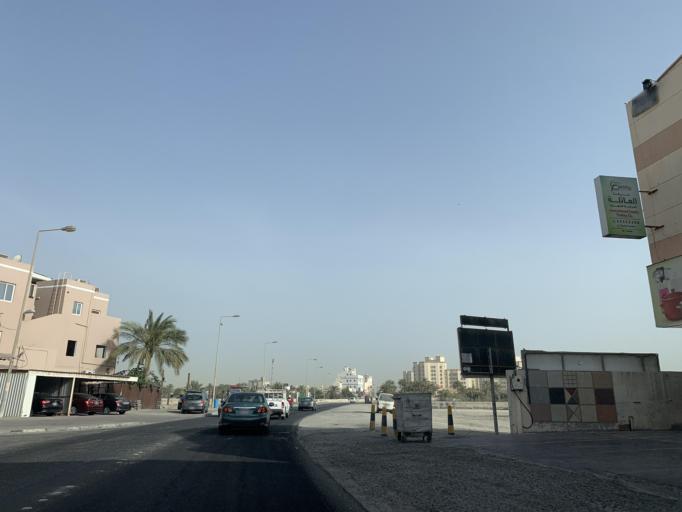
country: BH
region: Northern
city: Madinat `Isa
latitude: 26.1800
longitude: 50.5610
